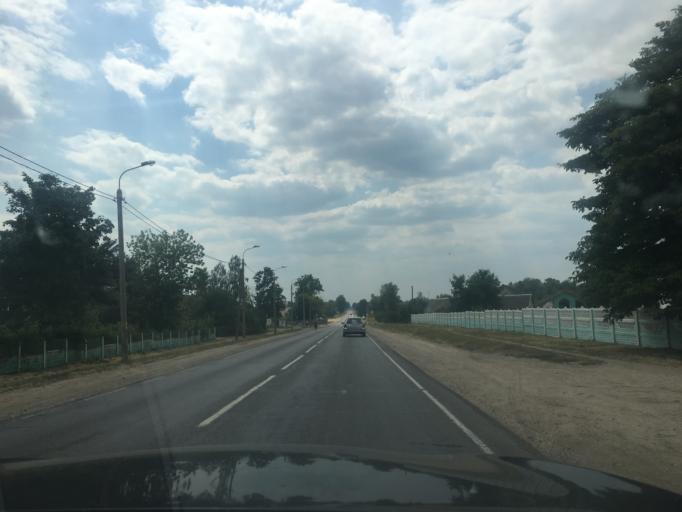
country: BY
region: Brest
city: Pruzhany
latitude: 52.5523
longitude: 24.4721
